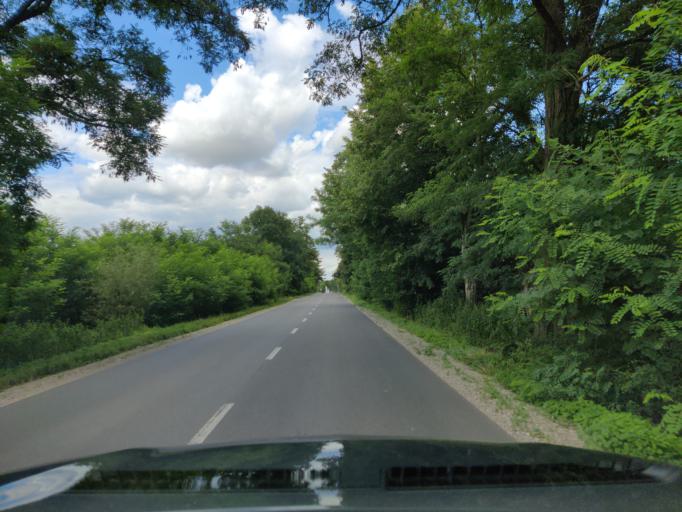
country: PL
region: Masovian Voivodeship
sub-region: Powiat wegrowski
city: Miedzna
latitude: 52.5359
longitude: 22.0864
